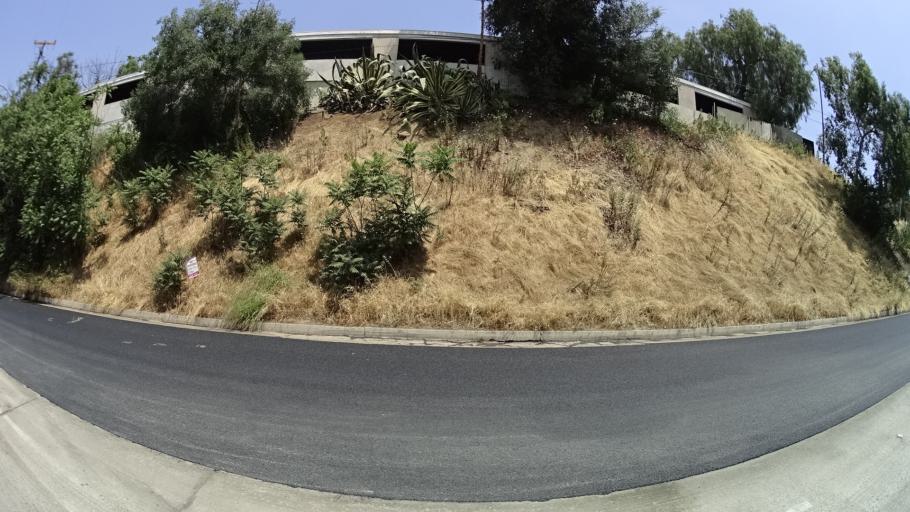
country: US
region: California
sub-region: Los Angeles County
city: Belvedere
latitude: 34.0636
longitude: -118.1539
